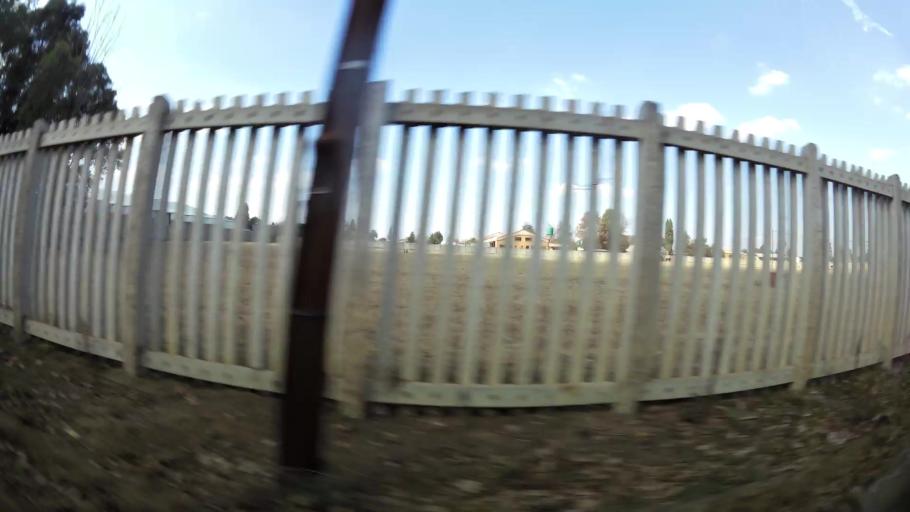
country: ZA
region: Gauteng
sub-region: Ekurhuleni Metropolitan Municipality
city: Benoni
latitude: -26.1067
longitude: 28.3645
